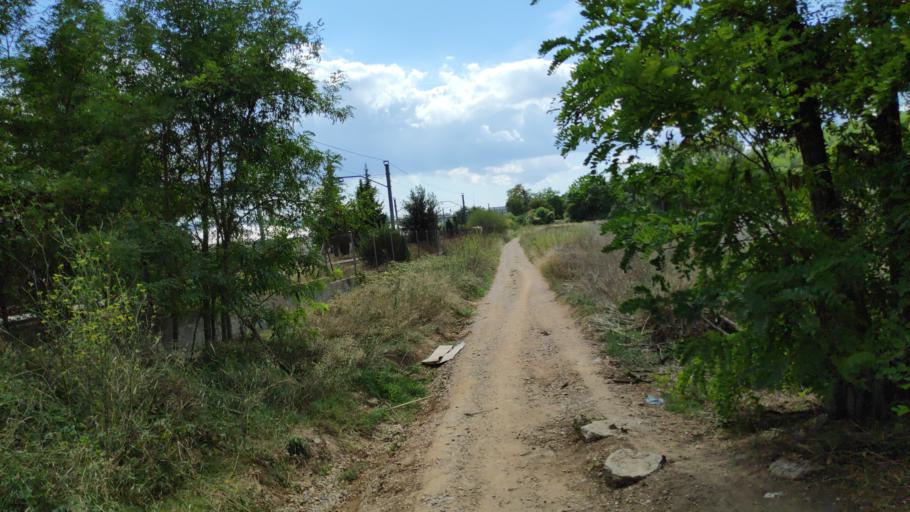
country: ES
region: Catalonia
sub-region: Provincia de Barcelona
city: Rubi
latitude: 41.5195
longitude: 2.0331
